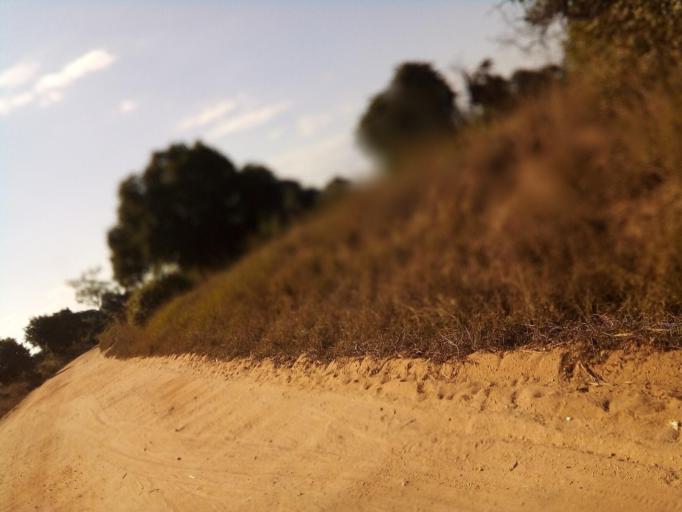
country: MZ
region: Zambezia
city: Quelimane
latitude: -17.5462
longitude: 36.6276
